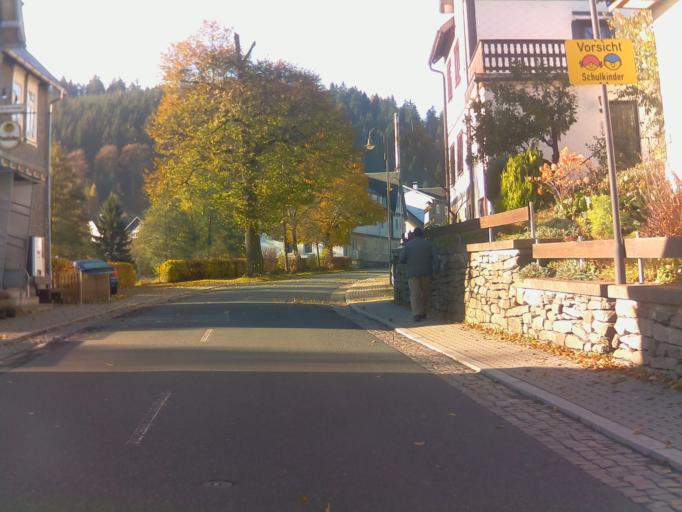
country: DE
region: Thuringia
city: Piesau
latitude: 50.5127
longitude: 11.2172
